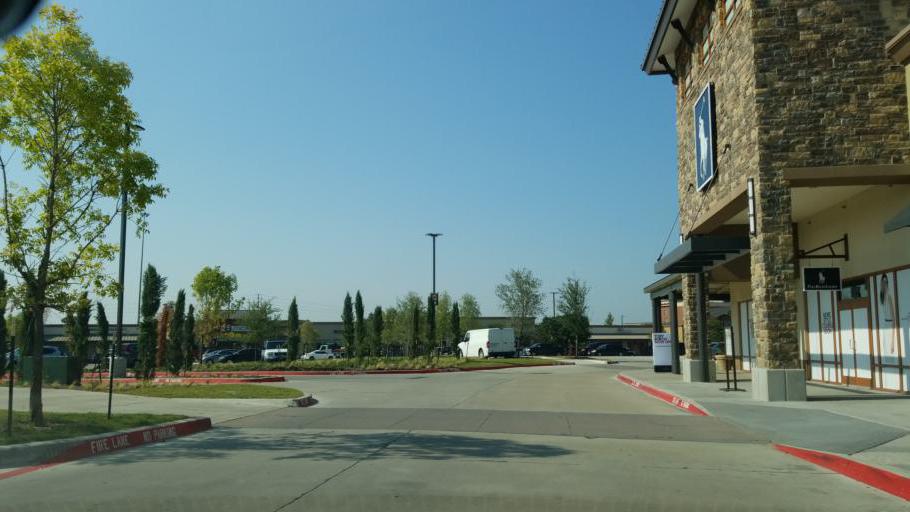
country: US
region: Texas
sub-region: Collin County
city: Allen
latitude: 33.1324
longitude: -96.6605
